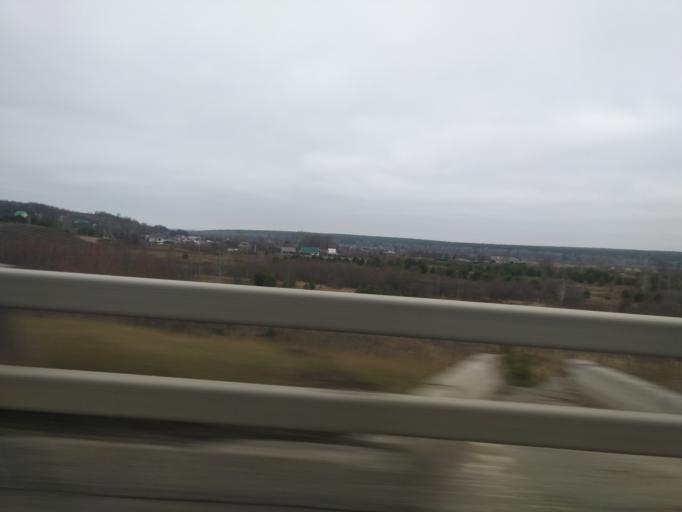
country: RU
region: Kirov
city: Sosnovka
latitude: 56.2338
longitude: 51.2212
